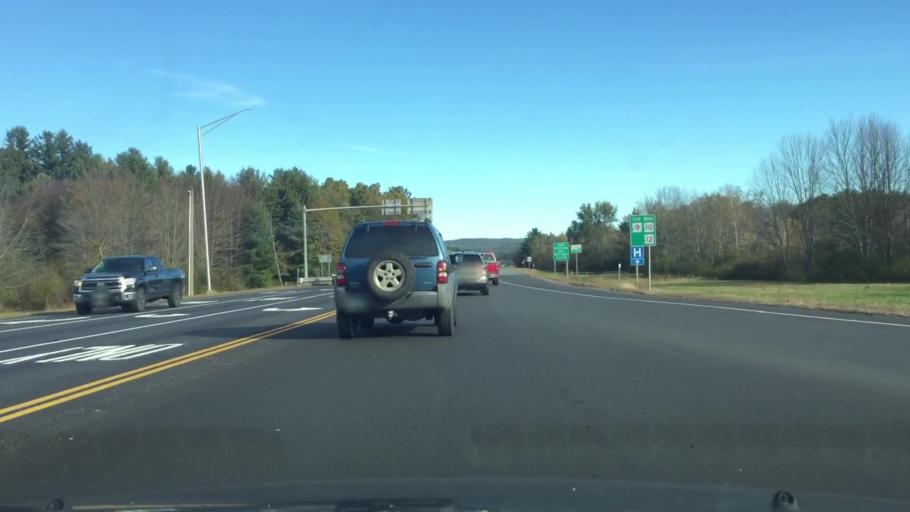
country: US
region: New Hampshire
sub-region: Cheshire County
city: Keene
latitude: 42.9235
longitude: -72.3001
